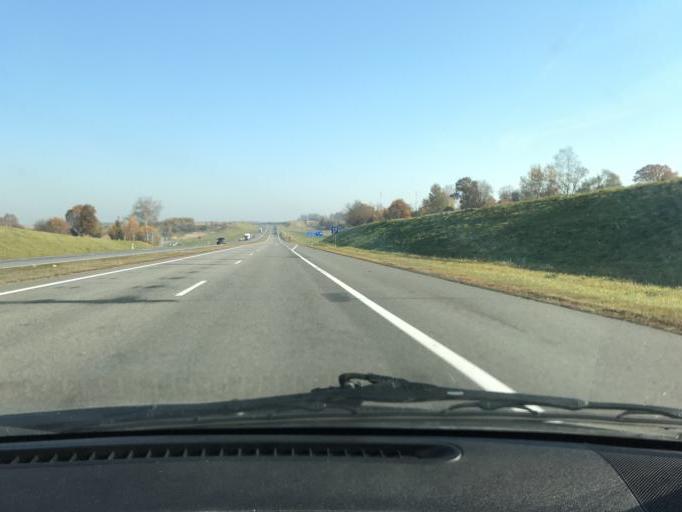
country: BY
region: Vitebsk
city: Baran'
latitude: 54.5659
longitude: 30.2997
